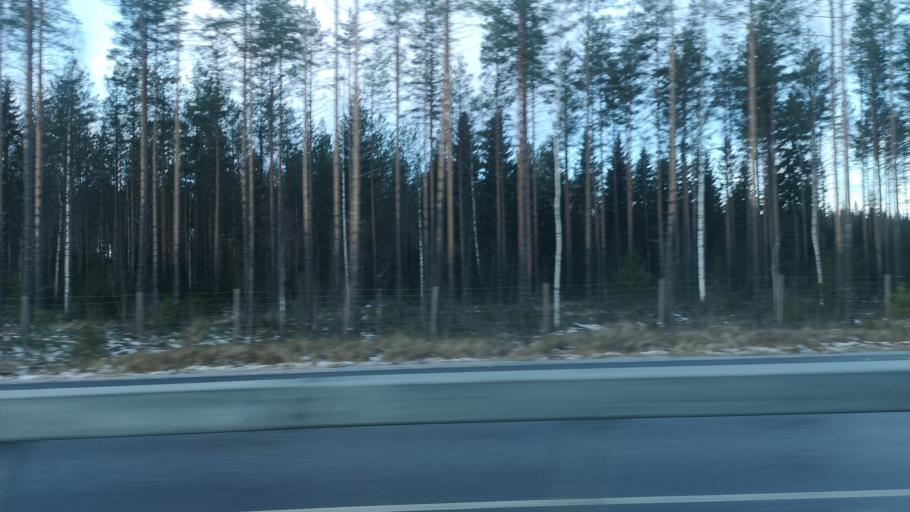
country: FI
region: Southern Savonia
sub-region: Mikkeli
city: Maentyharju
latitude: 61.4881
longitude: 26.7713
